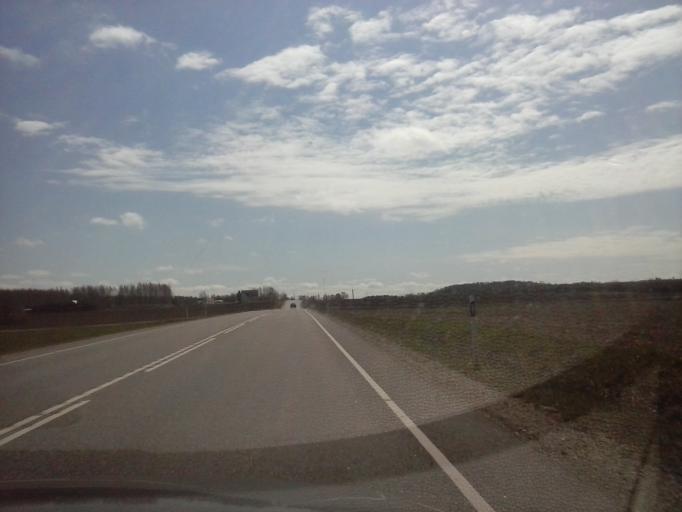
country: EE
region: Tartu
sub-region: UElenurme vald
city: Ulenurme
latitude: 58.2444
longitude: 26.6827
